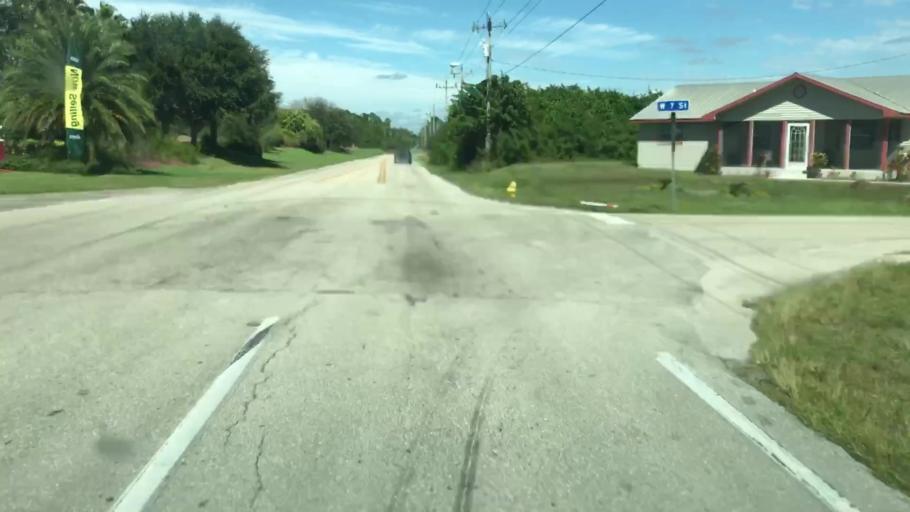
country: US
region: Florida
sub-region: Lee County
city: Lehigh Acres
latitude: 26.6246
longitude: -81.6463
